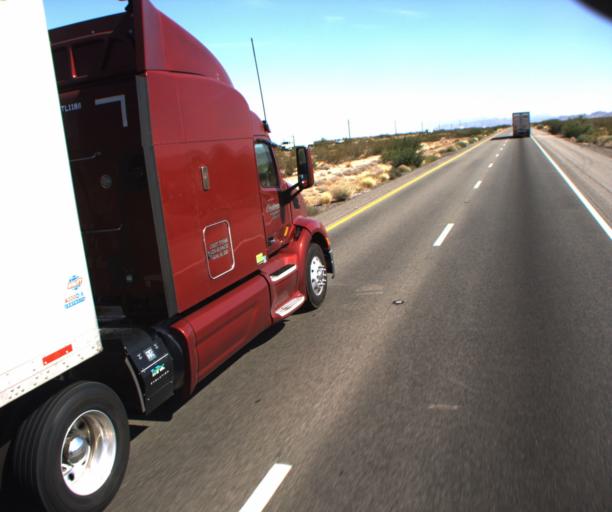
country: US
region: Arizona
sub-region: Mohave County
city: Kingman
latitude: 34.9503
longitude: -114.1458
